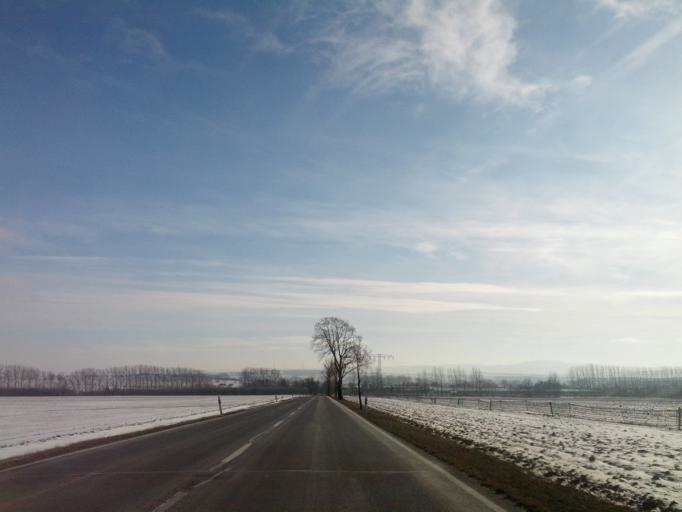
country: DE
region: Thuringia
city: Friedrichswerth
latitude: 51.0320
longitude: 10.5321
